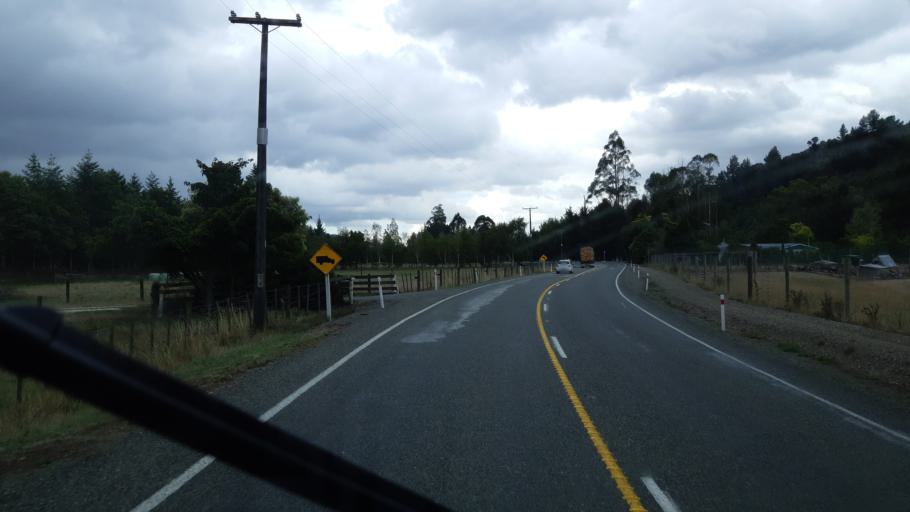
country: NZ
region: Tasman
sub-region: Tasman District
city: Wakefield
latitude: -41.4561
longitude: 172.9541
